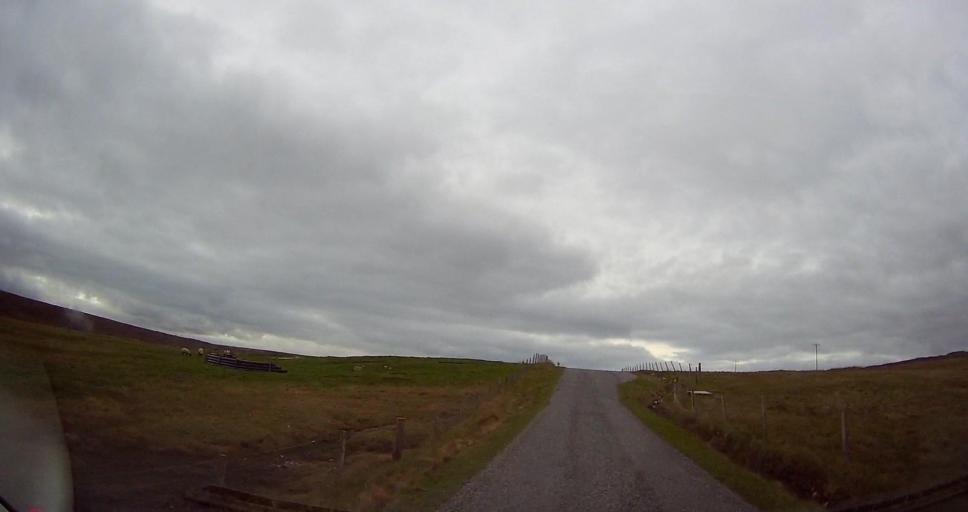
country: GB
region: Scotland
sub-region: Shetland Islands
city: Shetland
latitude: 60.5057
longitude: -1.1065
